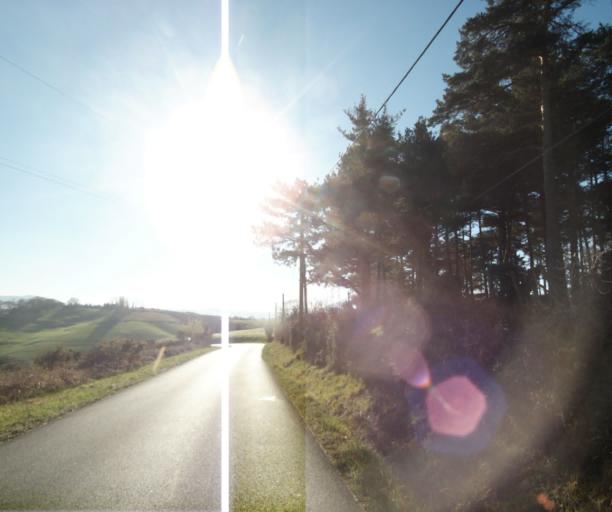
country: FR
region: Aquitaine
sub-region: Departement des Pyrenees-Atlantiques
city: Hendaye
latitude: 43.3562
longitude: -1.7454
